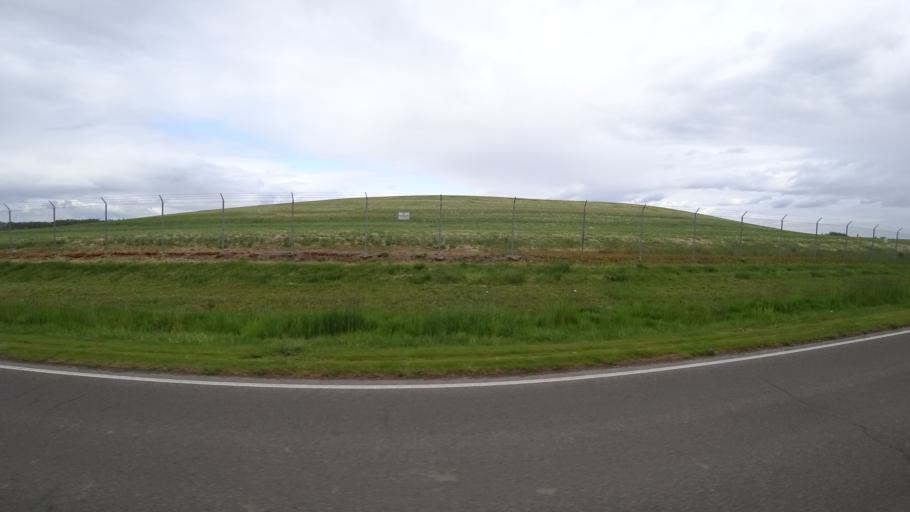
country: US
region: Oregon
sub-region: Washington County
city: Hillsboro
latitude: 45.5479
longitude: -122.9617
